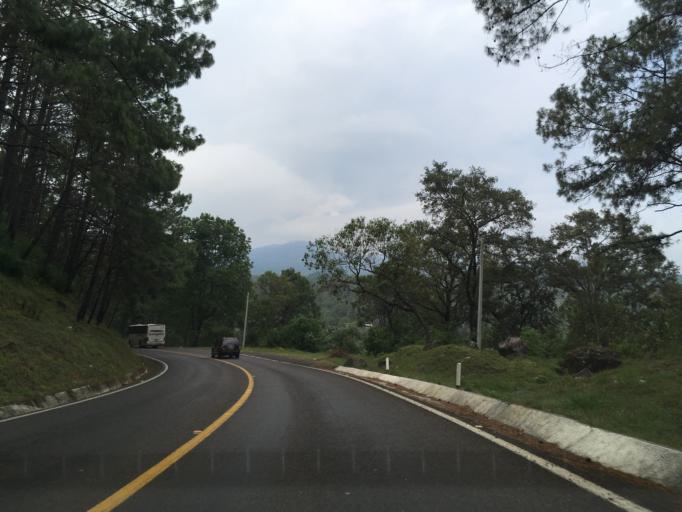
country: MX
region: Michoacan
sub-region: Uruapan
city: Toreo Bajo (El Toreo Bajo)
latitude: 19.4609
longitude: -101.9513
